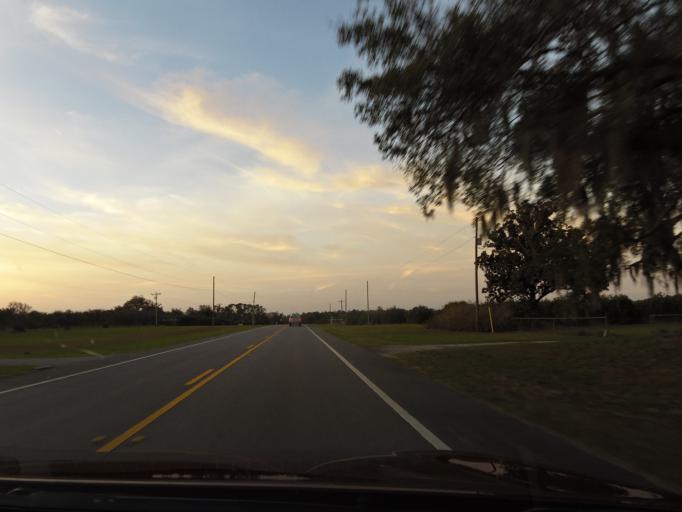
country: US
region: Florida
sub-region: Volusia County
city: De Leon Springs
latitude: 29.1582
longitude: -81.2953
